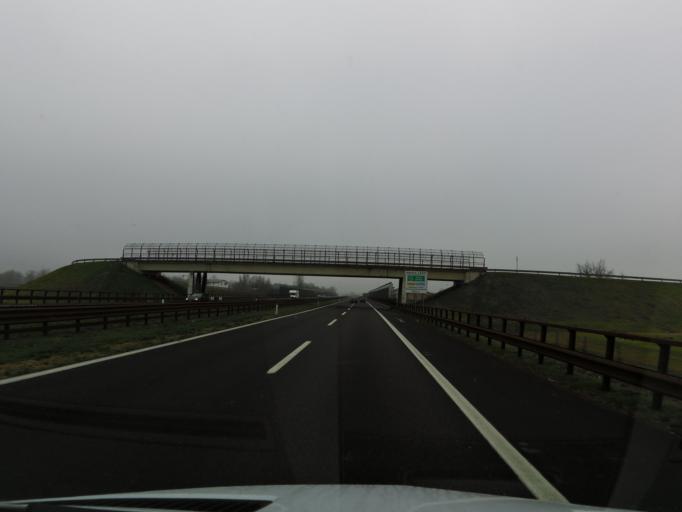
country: IT
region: Emilia-Romagna
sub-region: Provincia di Modena
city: Santa Croce Scuole
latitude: 44.7439
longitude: 10.8448
